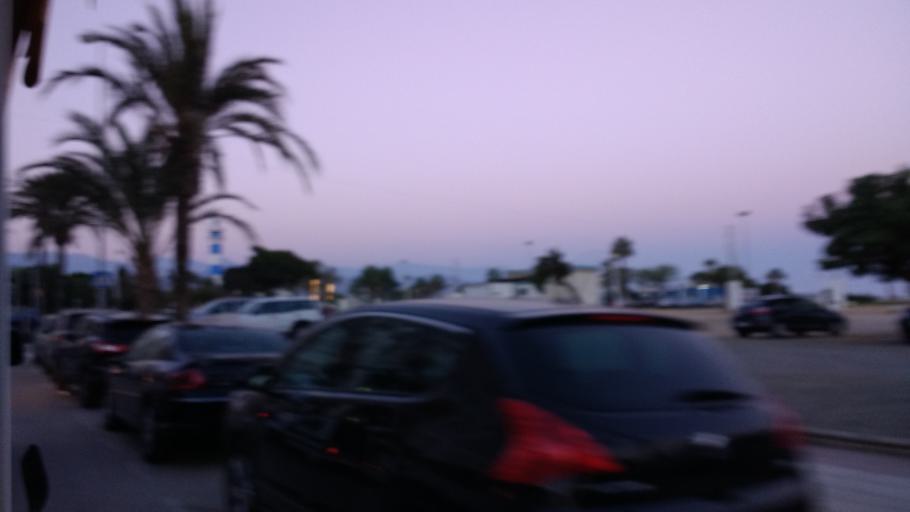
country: ES
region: Andalusia
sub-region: Provincia de Malaga
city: Velez-Malaga
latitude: 36.7338
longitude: -4.0980
